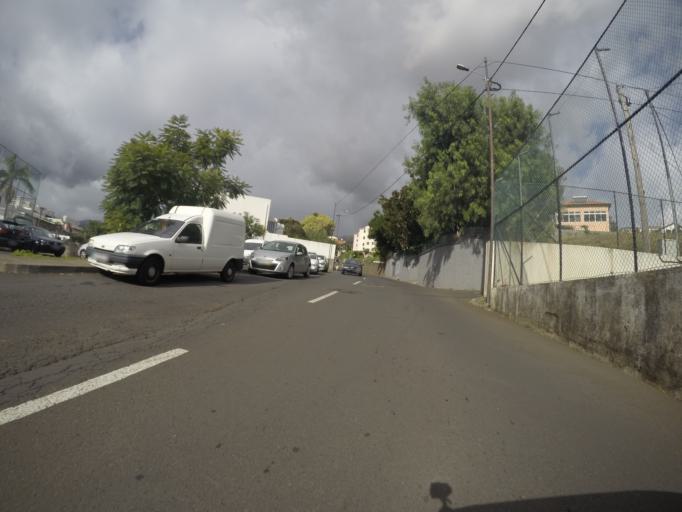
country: PT
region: Madeira
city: Camara de Lobos
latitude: 32.6584
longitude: -16.9441
